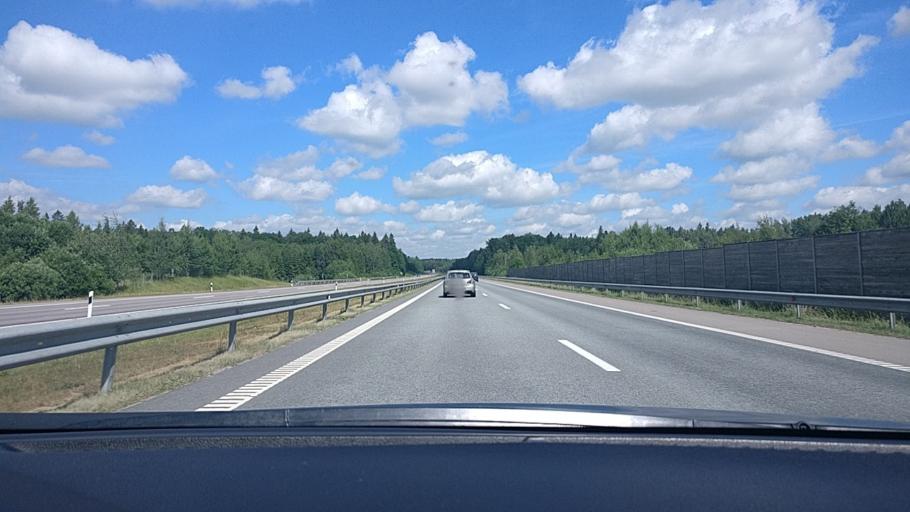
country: LT
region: Vilnius County
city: Pasilaiciai
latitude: 54.8352
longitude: 25.1197
